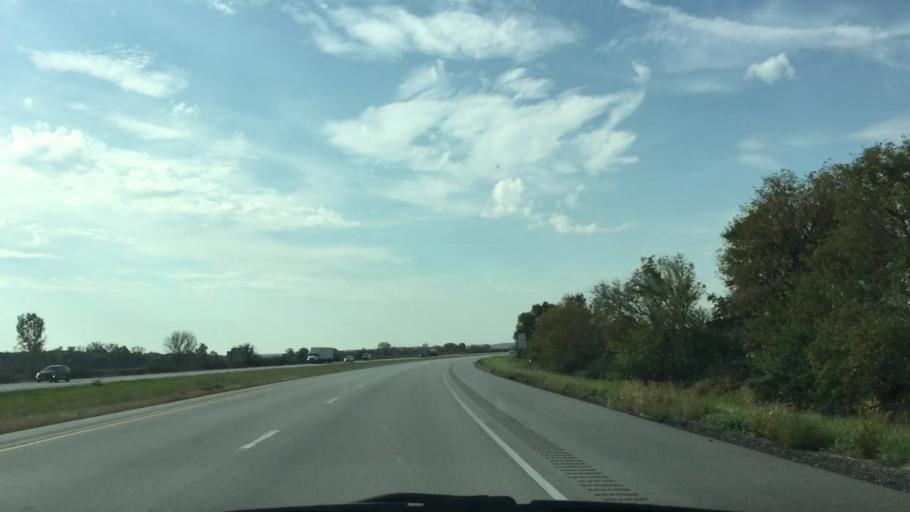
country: US
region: Illinois
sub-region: Whiteside County
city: Erie
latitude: 41.5998
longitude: -90.1924
